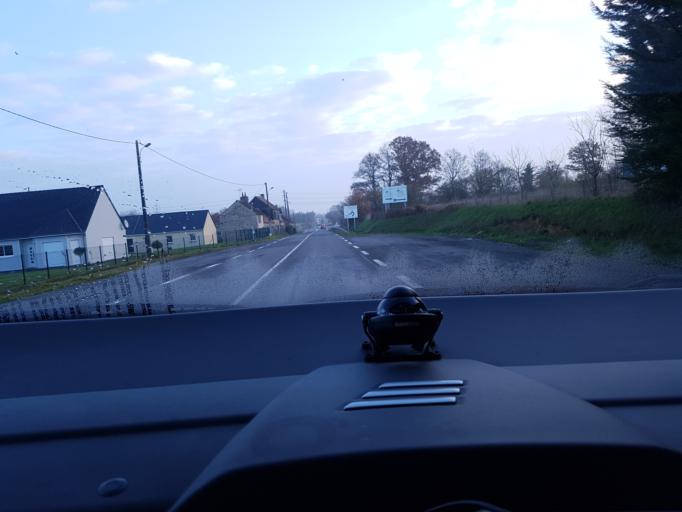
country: FR
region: Lower Normandy
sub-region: Departement de l'Orne
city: Domfront
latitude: 48.5917
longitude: -0.6267
